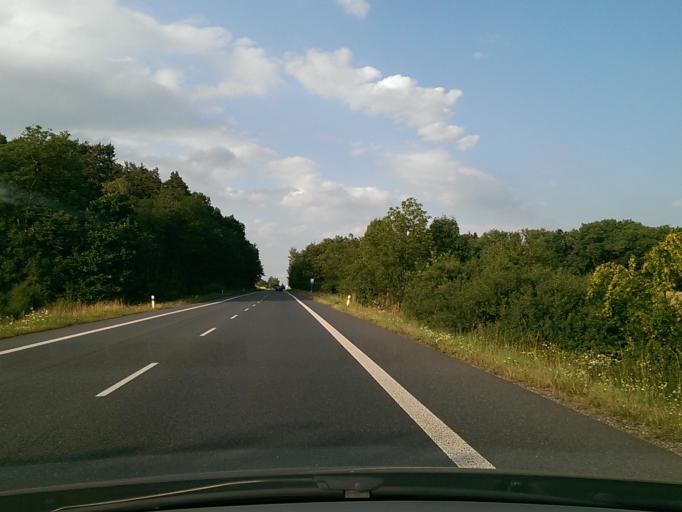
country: CZ
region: Central Bohemia
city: Dolni Bousov
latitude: 50.4507
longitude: 15.0828
